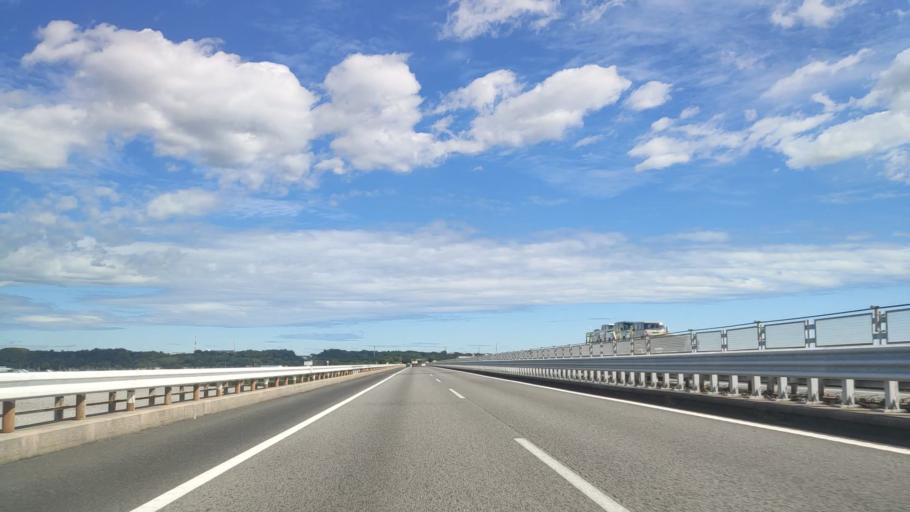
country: JP
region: Shizuoka
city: Iwata
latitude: 34.7473
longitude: 137.8133
